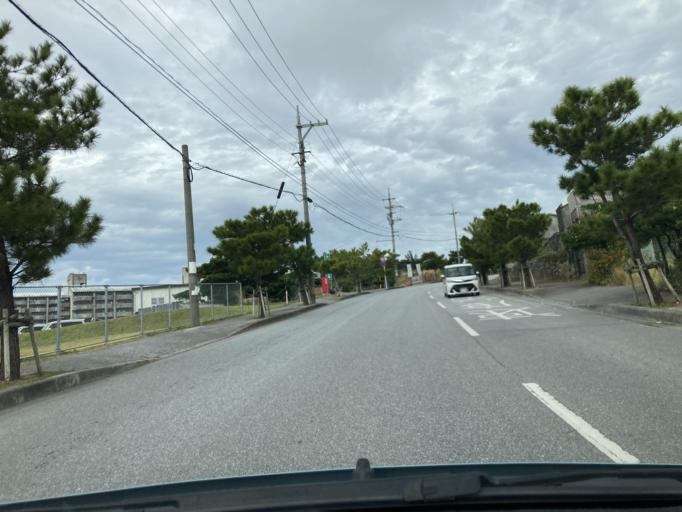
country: JP
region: Okinawa
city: Naha-shi
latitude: 26.2147
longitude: 127.7301
